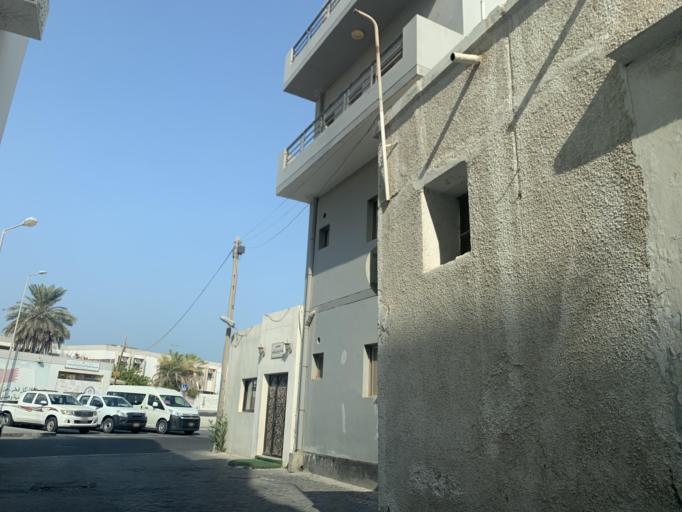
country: BH
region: Muharraq
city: Al Hadd
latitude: 26.2730
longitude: 50.6529
